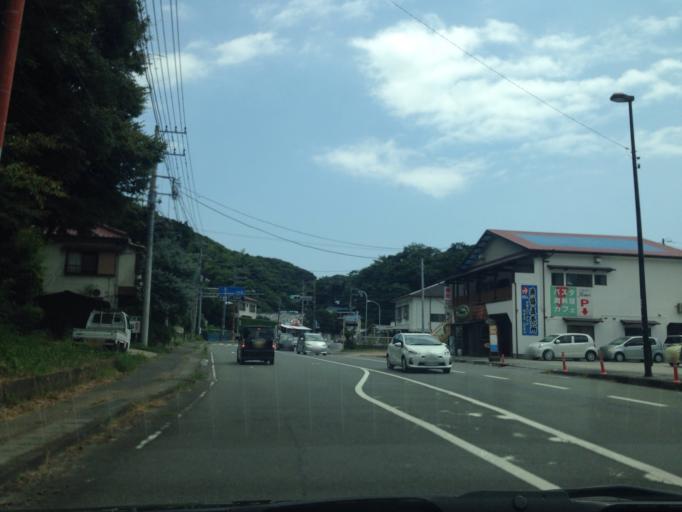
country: JP
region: Shizuoka
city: Shimoda
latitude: 34.6429
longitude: 138.8868
